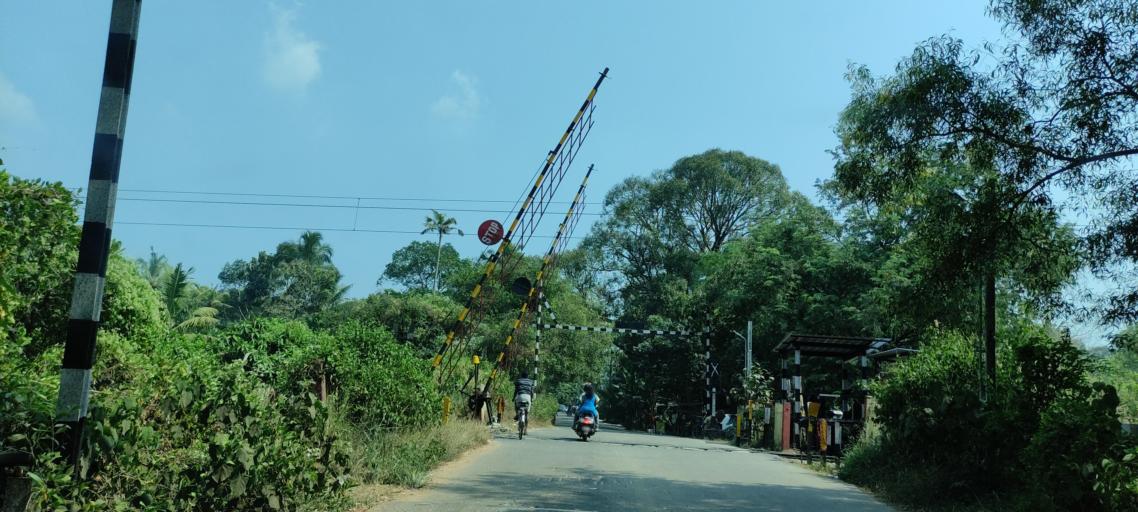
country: IN
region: Kerala
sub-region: Alappuzha
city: Shertallai
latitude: 9.6017
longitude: 76.3186
